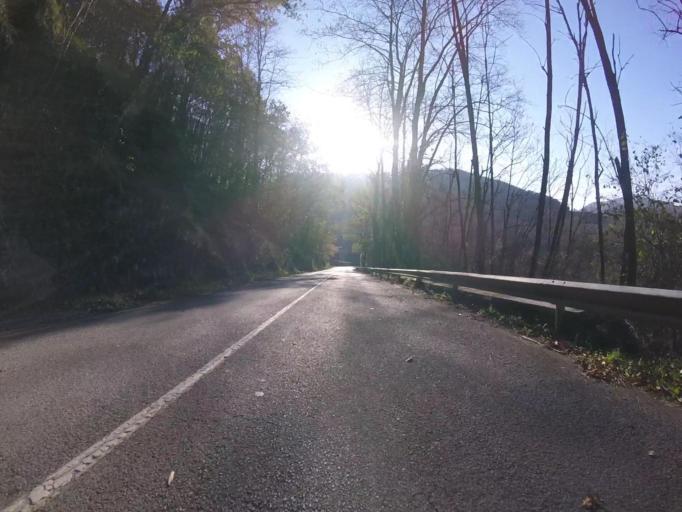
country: ES
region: Navarre
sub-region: Provincia de Navarra
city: Lesaka
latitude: 43.2405
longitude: -1.6734
